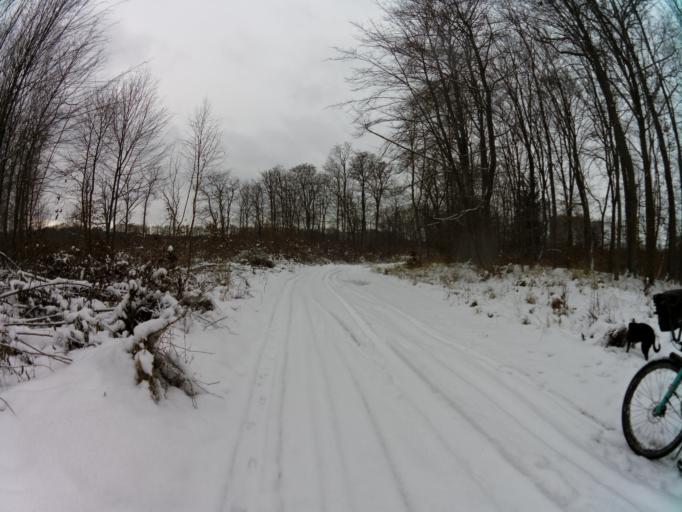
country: PL
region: West Pomeranian Voivodeship
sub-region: Powiat choszczenski
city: Recz
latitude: 53.3231
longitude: 15.5504
